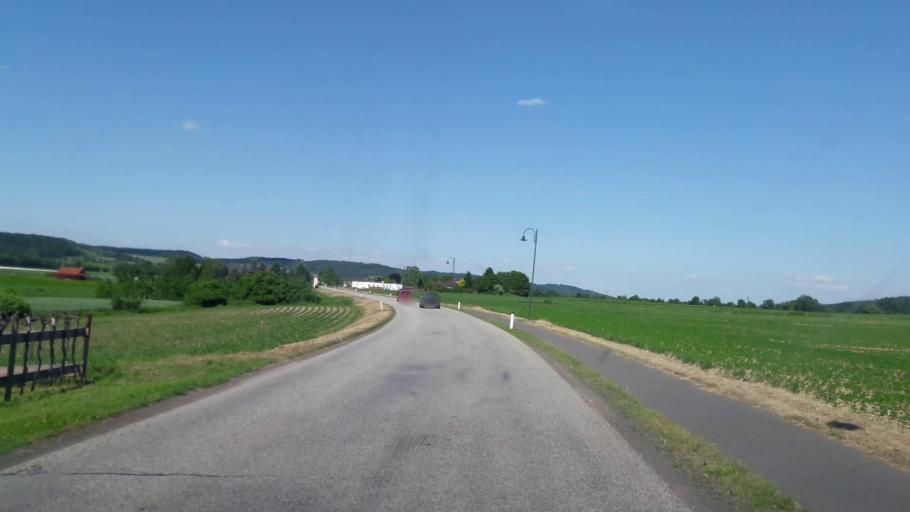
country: AT
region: Styria
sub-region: Politischer Bezirk Suedoststeiermark
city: Fehring
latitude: 46.9347
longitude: 16.0323
